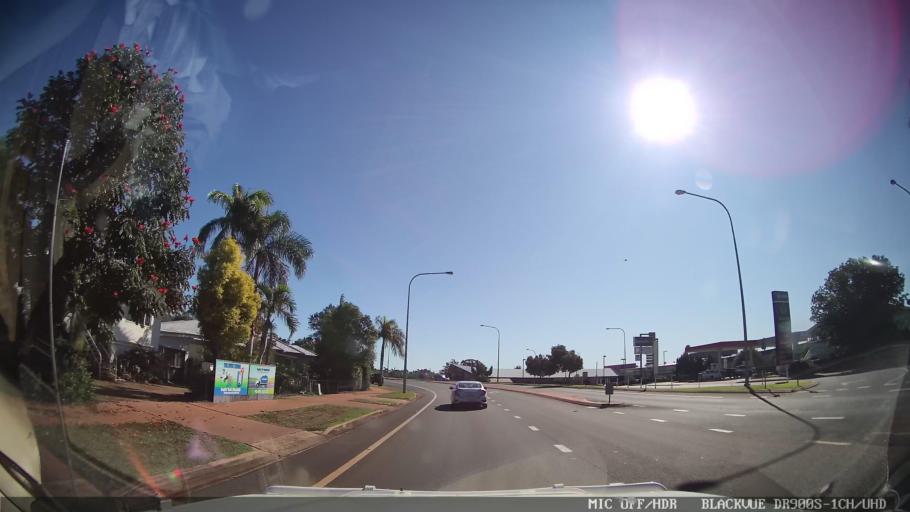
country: AU
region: Queensland
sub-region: Bundaberg
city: Childers
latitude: -25.2330
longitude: 152.2716
